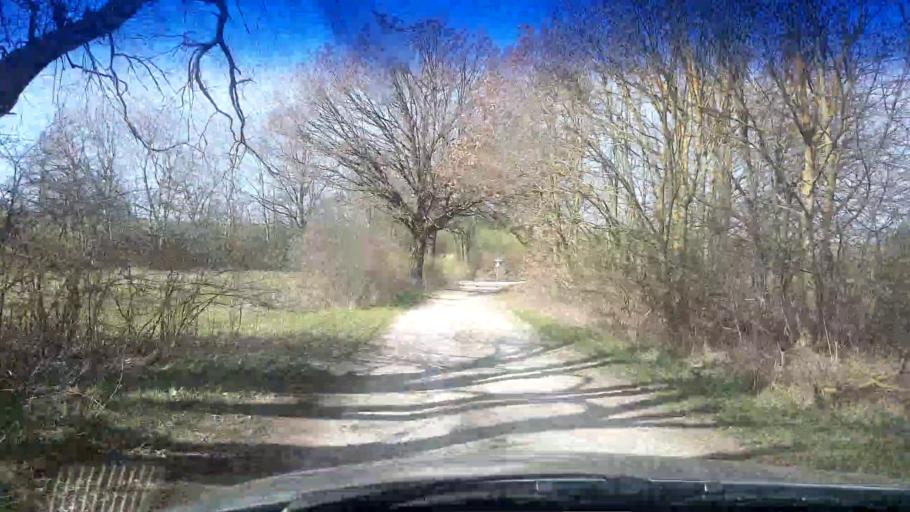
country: DE
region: Bavaria
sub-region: Upper Franconia
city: Bischberg
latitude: 49.8979
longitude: 10.8265
